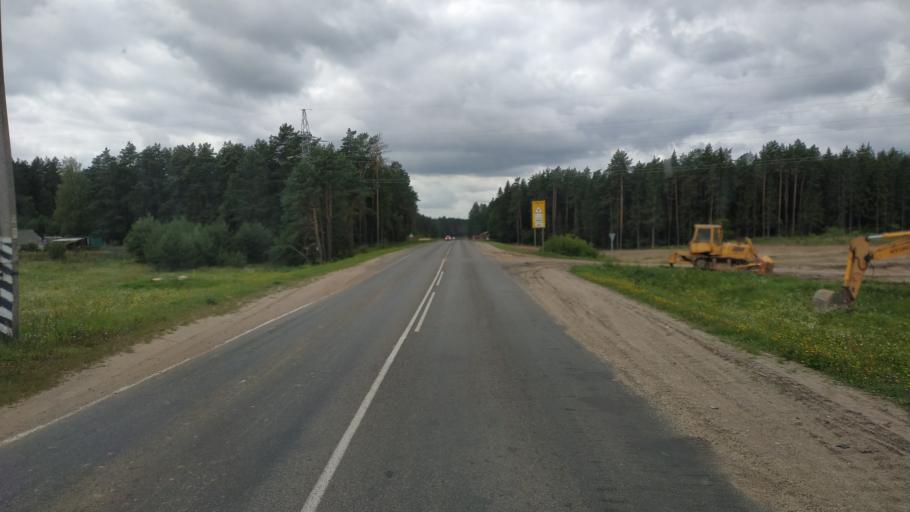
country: BY
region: Mogilev
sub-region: Mahilyowski Rayon
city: Veyno
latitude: 53.8760
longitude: 30.4273
